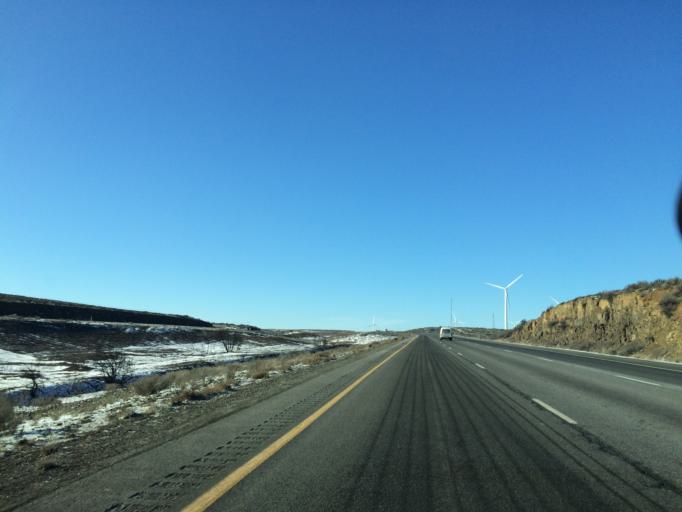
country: US
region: Washington
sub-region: Kittitas County
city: Kittitas
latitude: 46.9448
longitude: -120.1858
